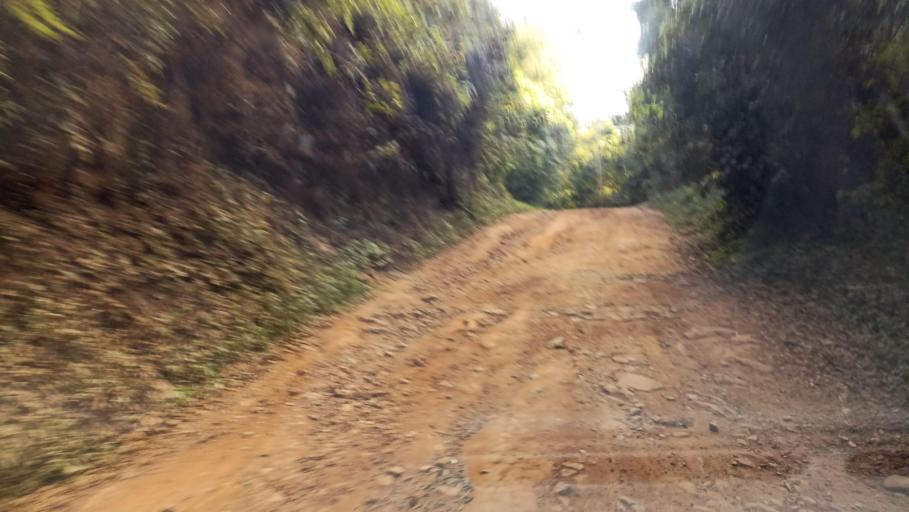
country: BR
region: Minas Gerais
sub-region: Ouro Preto
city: Ouro Preto
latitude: -20.3041
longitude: -43.5760
